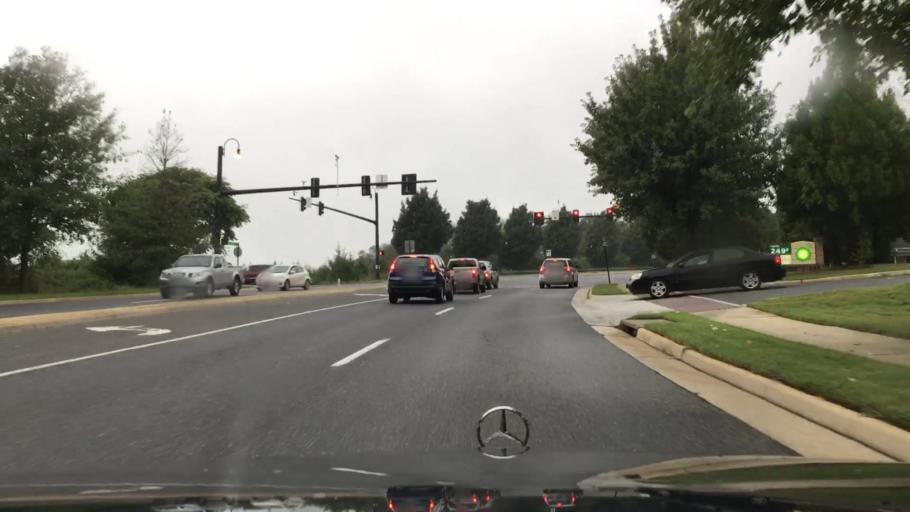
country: US
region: Virginia
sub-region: Campbell County
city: Timberlake
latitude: 37.3617
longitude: -79.2449
